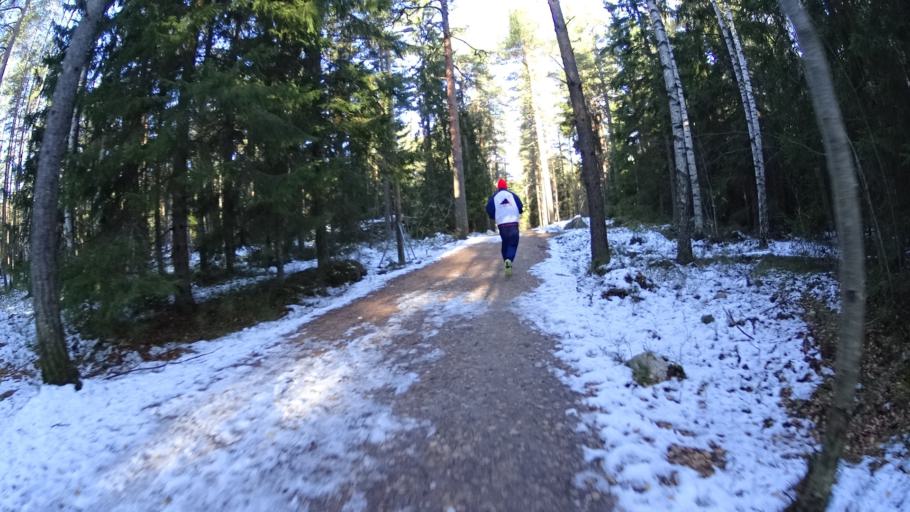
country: FI
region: Uusimaa
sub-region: Helsinki
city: Kauniainen
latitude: 60.2153
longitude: 24.6974
